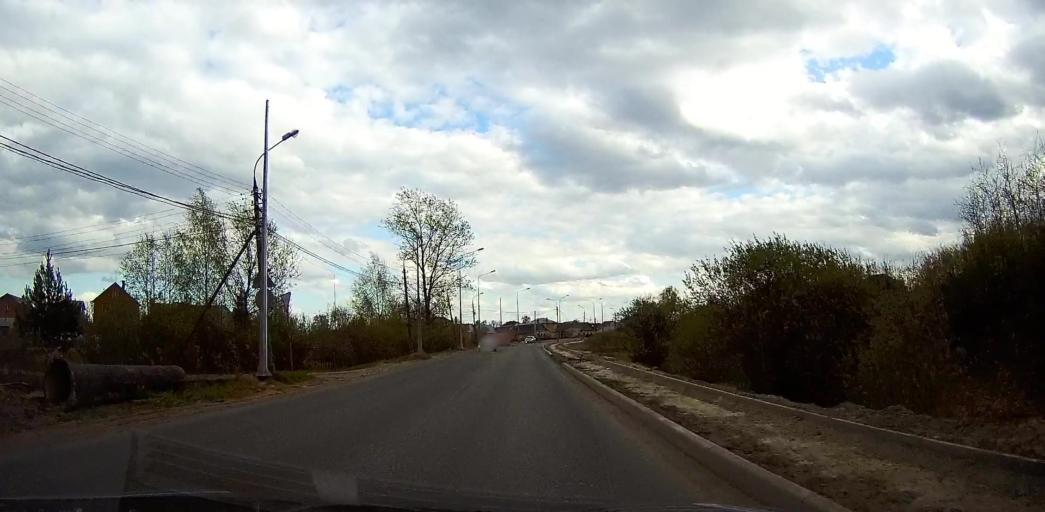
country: RU
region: Moskovskaya
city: Pavlovskiy Posad
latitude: 55.7974
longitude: 38.6883
